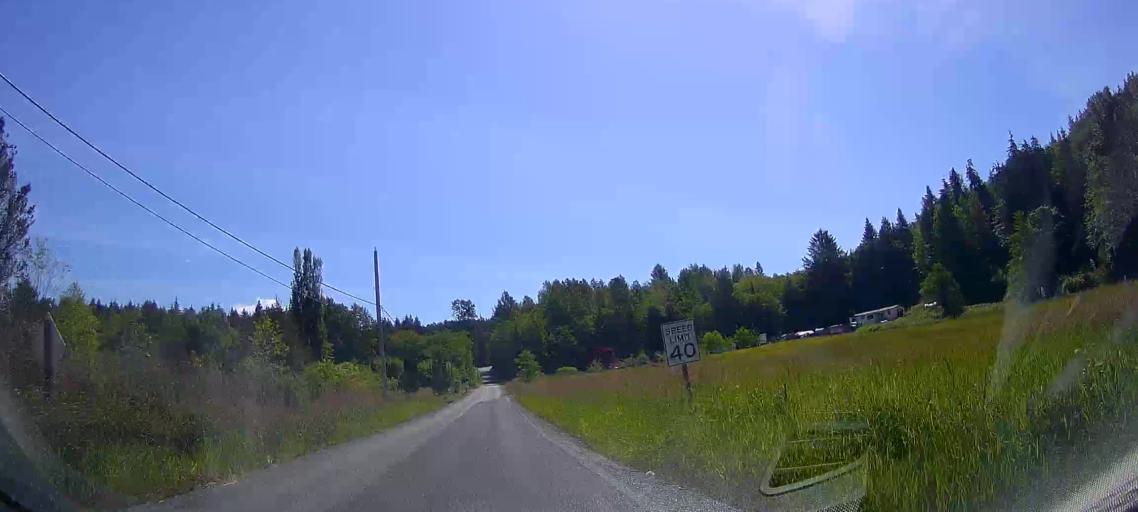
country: US
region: Washington
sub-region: Skagit County
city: Sedro-Woolley
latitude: 48.5542
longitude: -122.2870
